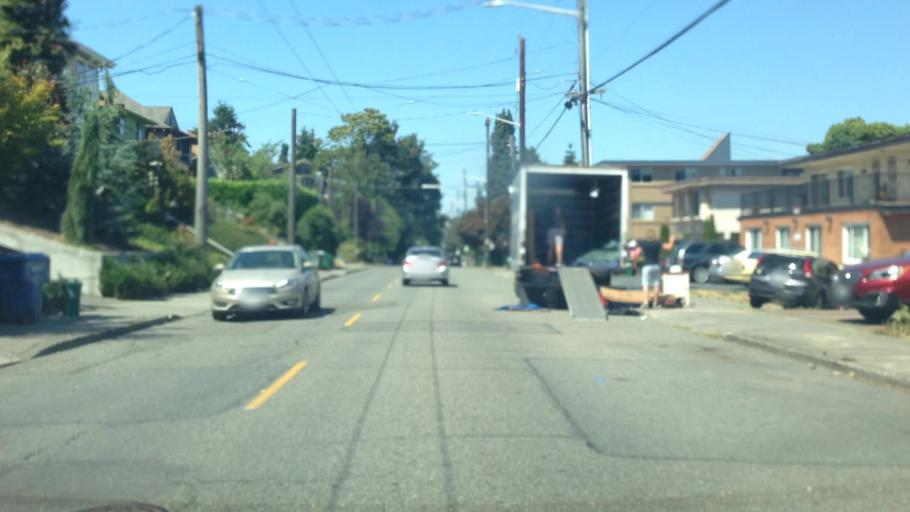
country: US
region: Washington
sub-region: King County
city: Seattle
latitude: 47.5892
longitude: -122.3149
